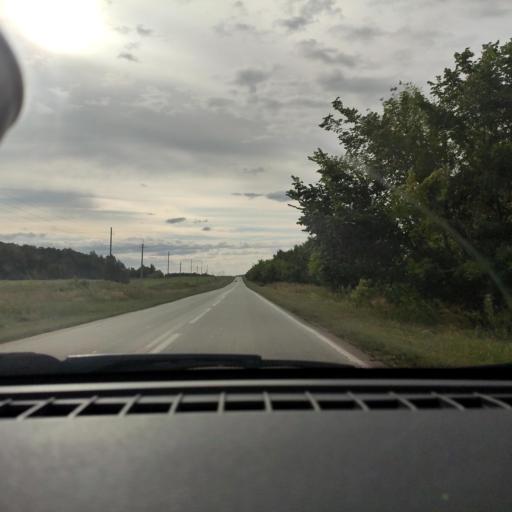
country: RU
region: Samara
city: Georgiyevka
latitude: 53.4282
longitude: 50.7969
